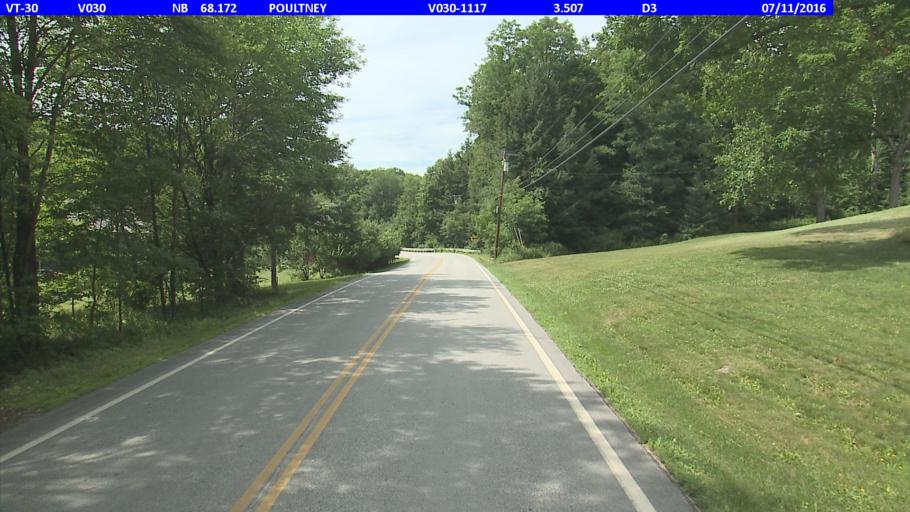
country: US
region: Vermont
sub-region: Rutland County
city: Poultney
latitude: 43.5097
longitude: -73.2171
